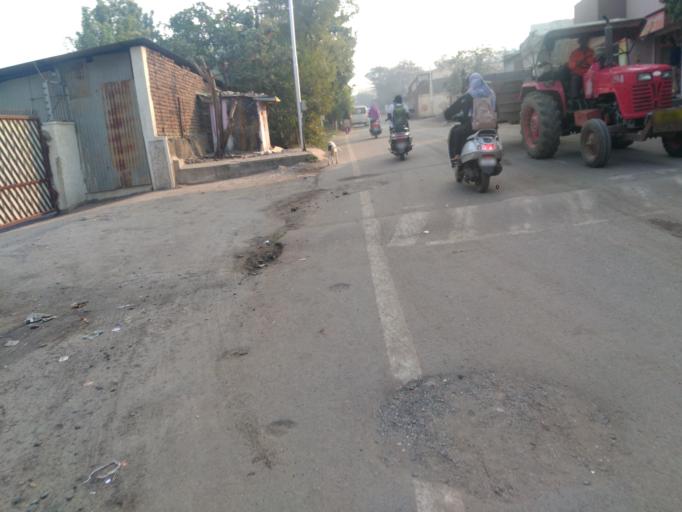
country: IN
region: Maharashtra
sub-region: Pune Division
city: Pune
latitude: 18.4356
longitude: 73.8930
